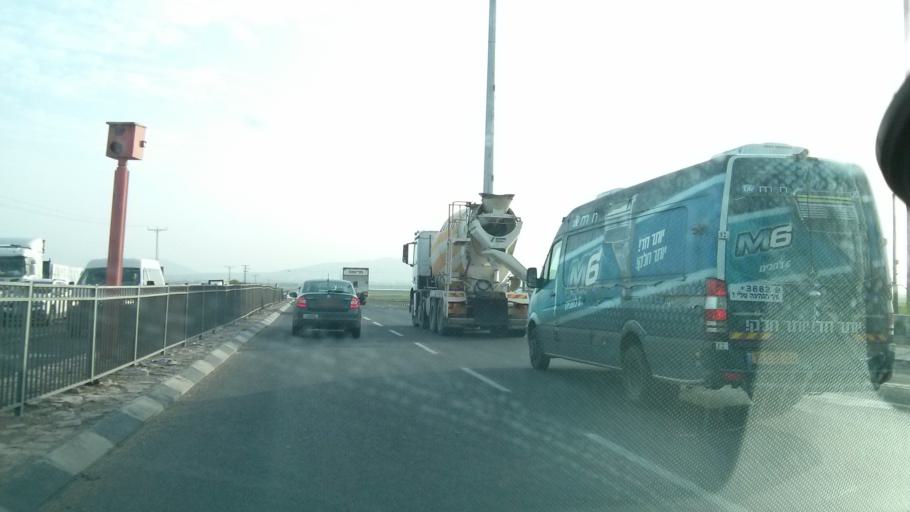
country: PS
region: West Bank
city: Zububah
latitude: 32.5729
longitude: 35.1921
